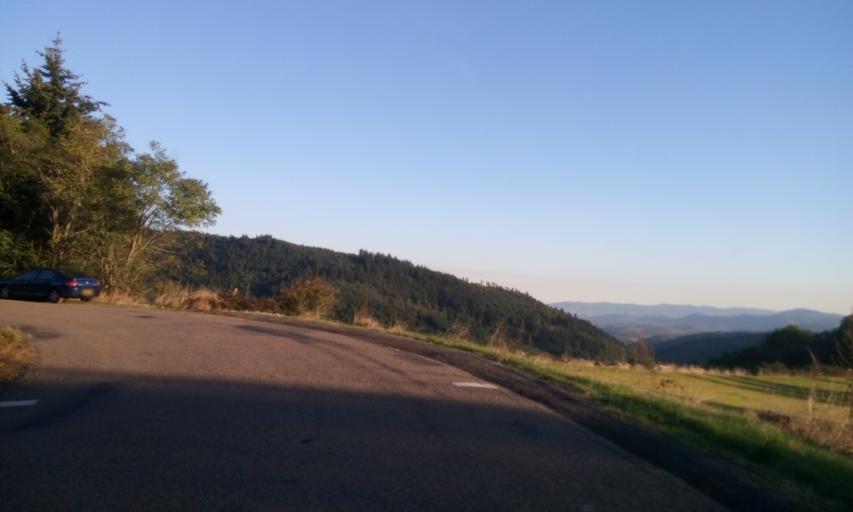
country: FR
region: Rhone-Alpes
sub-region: Departement du Rhone
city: Tarare
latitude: 45.9629
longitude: 4.4610
